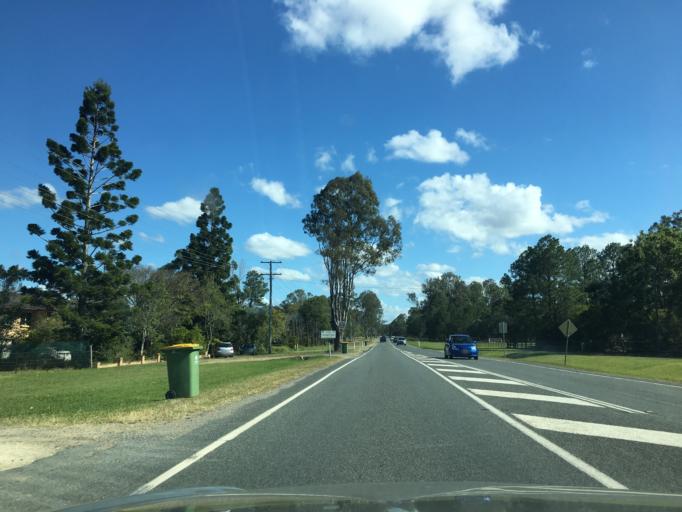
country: AU
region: Queensland
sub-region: Logan
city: Waterford West
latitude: -27.7175
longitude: 153.1287
